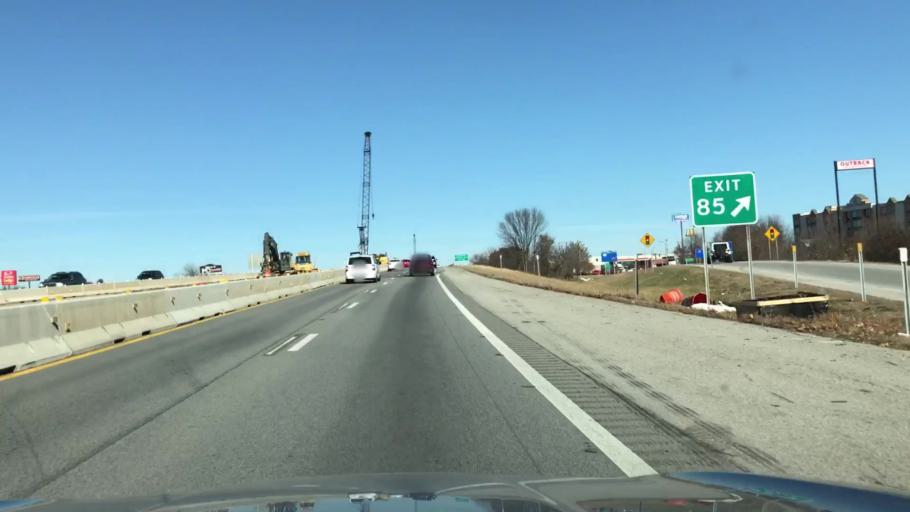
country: US
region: Arkansas
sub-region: Benton County
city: Bentonville
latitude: 36.3322
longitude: -94.1841
